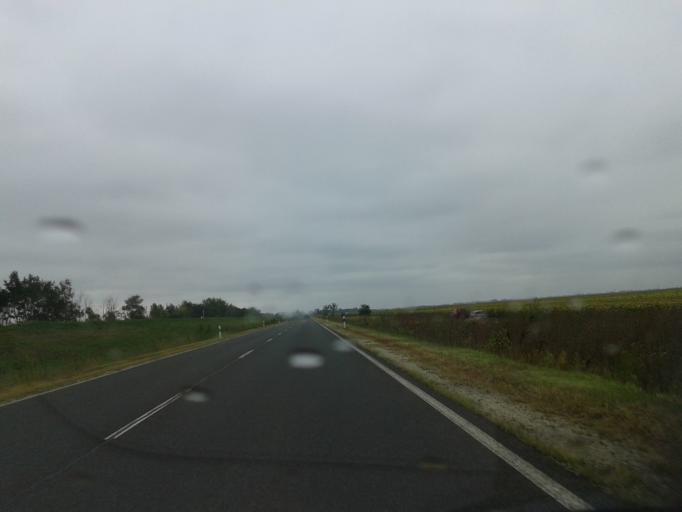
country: HU
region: Bacs-Kiskun
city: Harta
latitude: 46.7391
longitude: 19.0120
